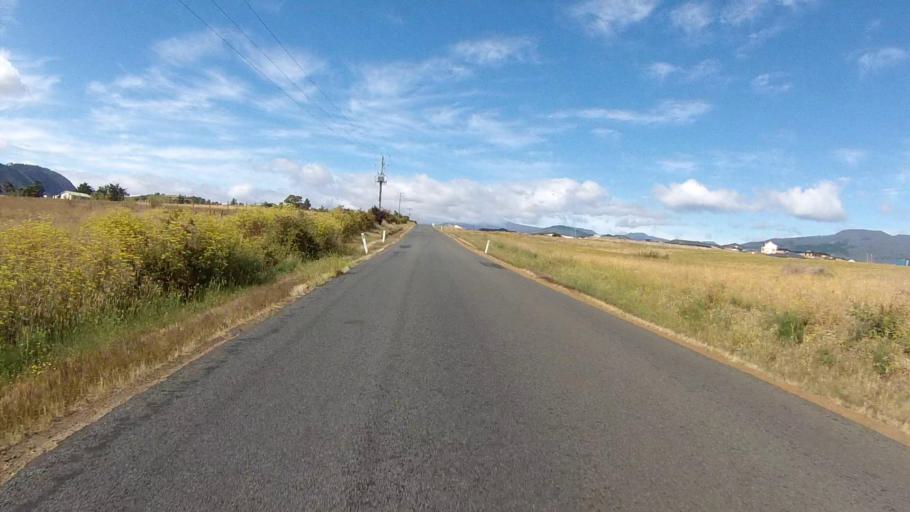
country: AU
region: Tasmania
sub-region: Brighton
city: Old Beach
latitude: -42.7595
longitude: 147.2798
